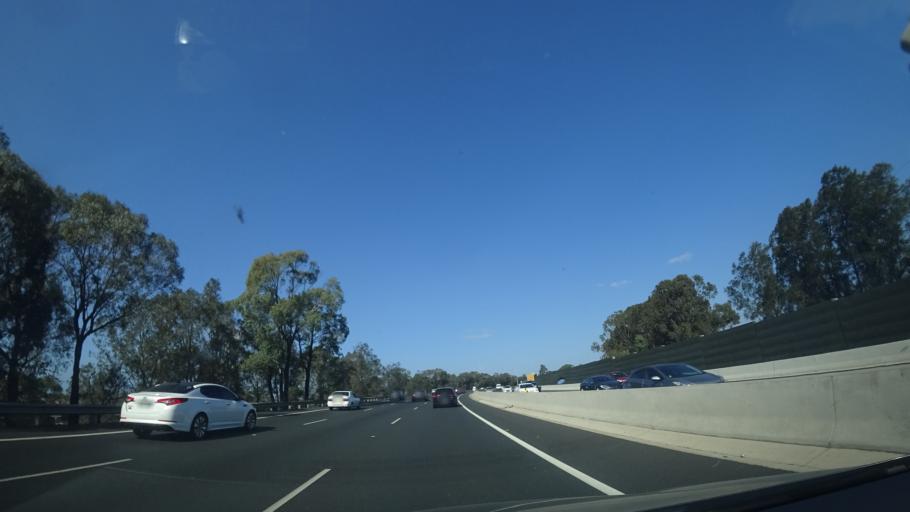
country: AU
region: New South Wales
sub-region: Bankstown
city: Revesby
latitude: -33.9398
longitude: 151.0069
